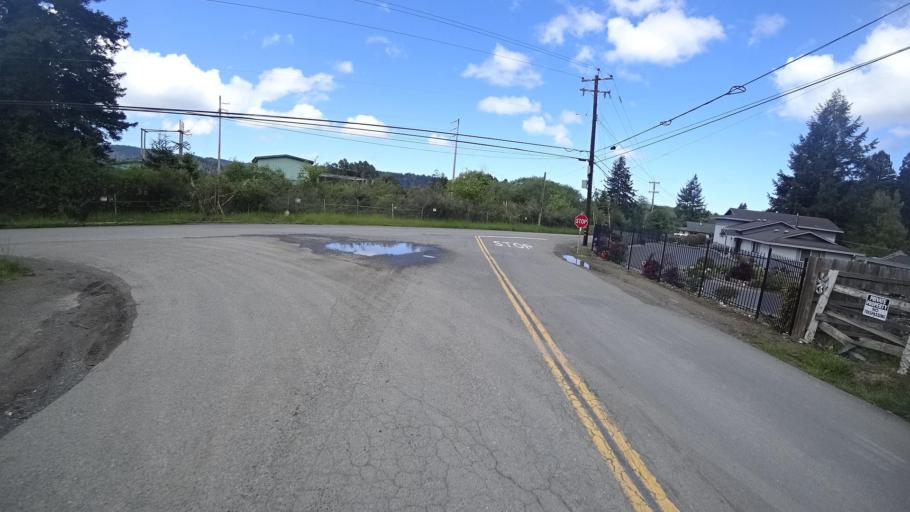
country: US
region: California
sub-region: Humboldt County
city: Blue Lake
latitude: 40.8975
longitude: -124.0074
